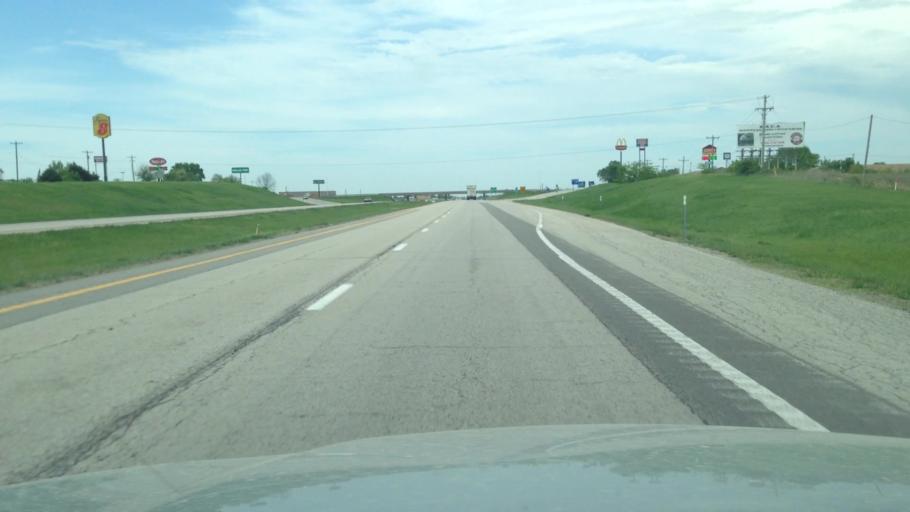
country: US
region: Missouri
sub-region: Harrison County
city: Bethany
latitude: 40.2602
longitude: -94.0127
